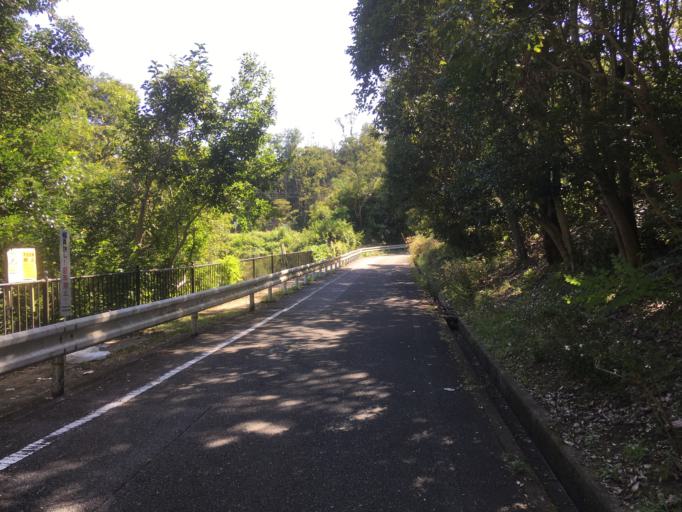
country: JP
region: Osaka
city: Daitocho
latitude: 34.7293
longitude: 135.6711
